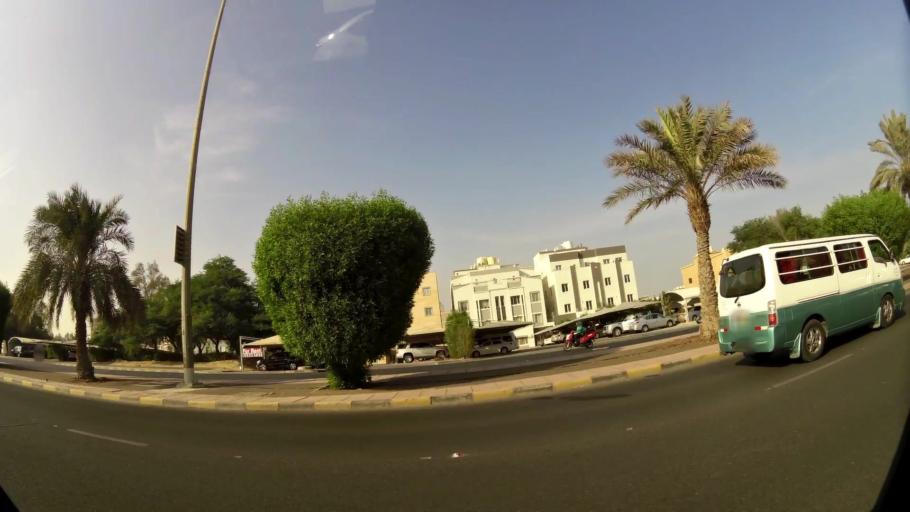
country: KW
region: Mubarak al Kabir
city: Mubarak al Kabir
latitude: 29.1749
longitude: 48.0946
